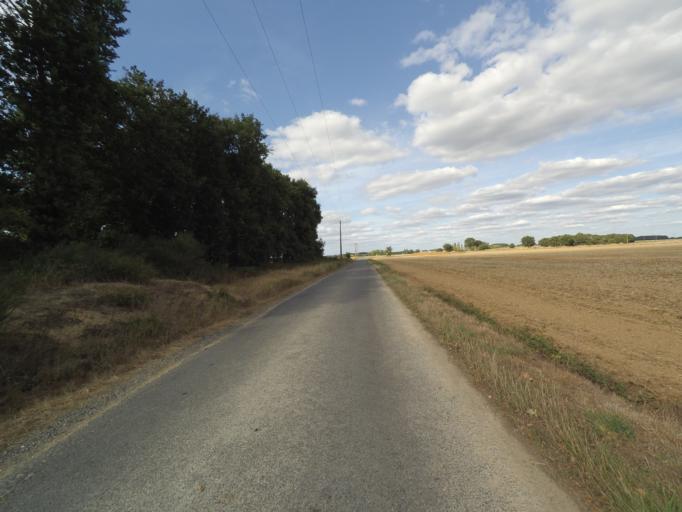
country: FR
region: Pays de la Loire
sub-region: Departement de la Loire-Atlantique
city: Vieillevigne
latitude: 46.9749
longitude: -1.3881
